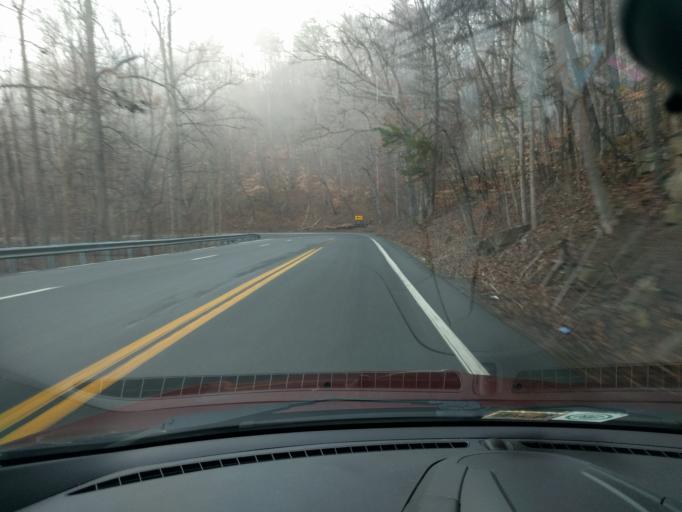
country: US
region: West Virginia
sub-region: Fayette County
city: Ansted
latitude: 38.1298
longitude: -81.1444
